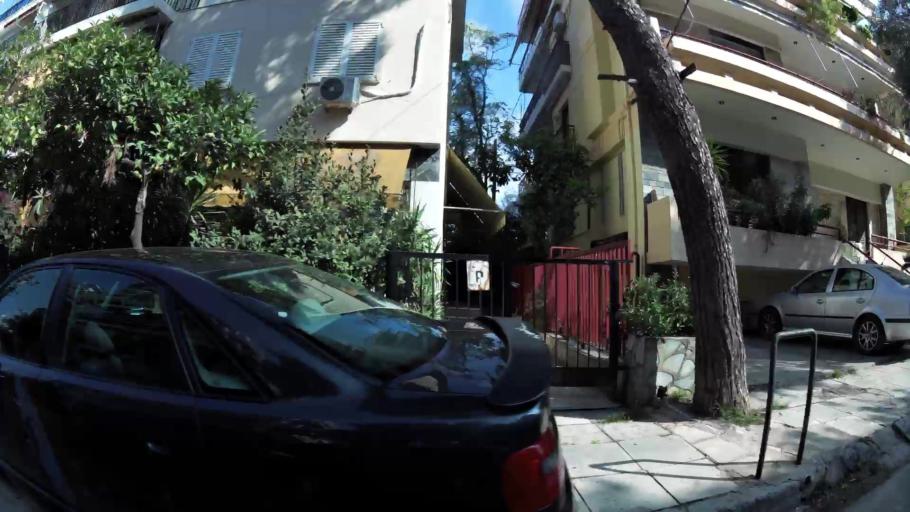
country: GR
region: Attica
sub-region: Nomarchia Athinas
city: Cholargos
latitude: 37.9993
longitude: 23.7920
